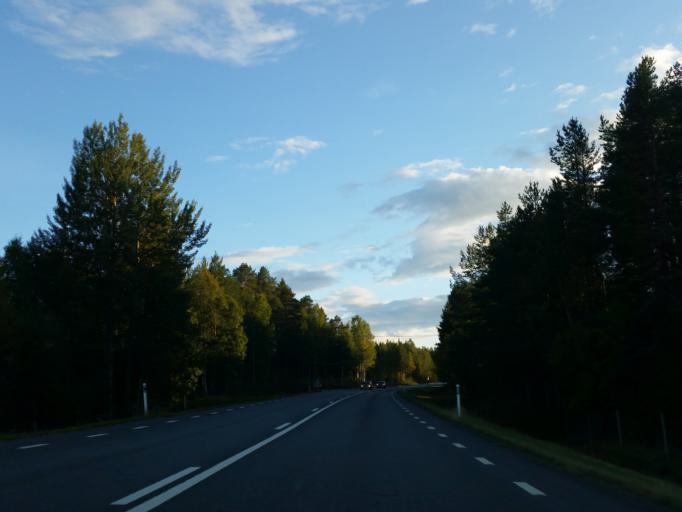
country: SE
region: Vaesterbotten
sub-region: Robertsfors Kommun
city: Robertsfors
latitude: 64.0210
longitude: 20.8382
